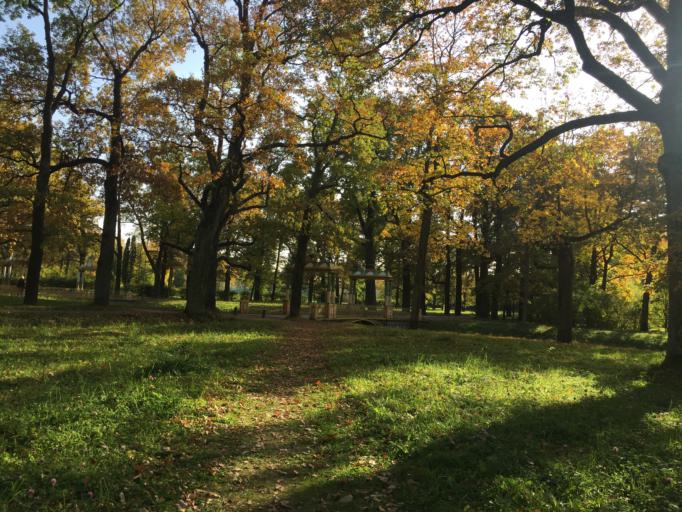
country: RU
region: St.-Petersburg
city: Pushkin
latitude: 59.7170
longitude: 30.3868
